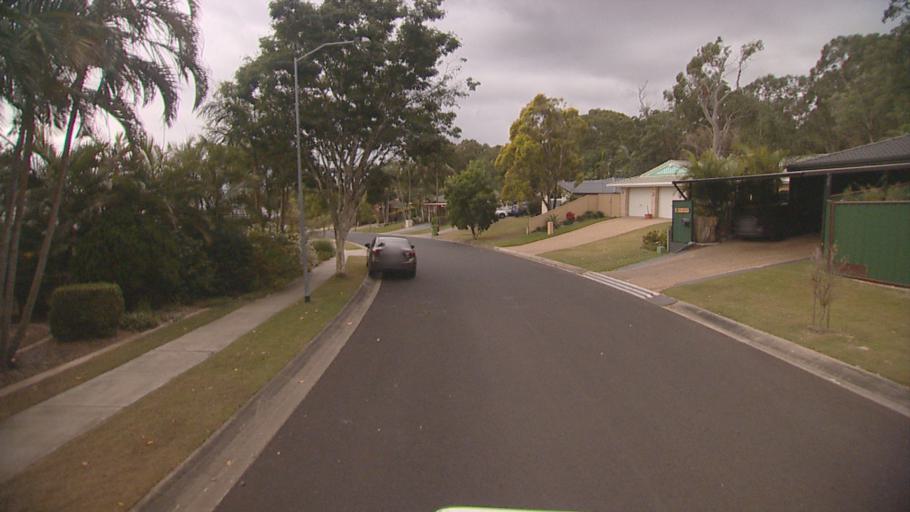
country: AU
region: Queensland
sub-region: Logan
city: Park Ridge South
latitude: -27.6777
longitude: 153.0581
